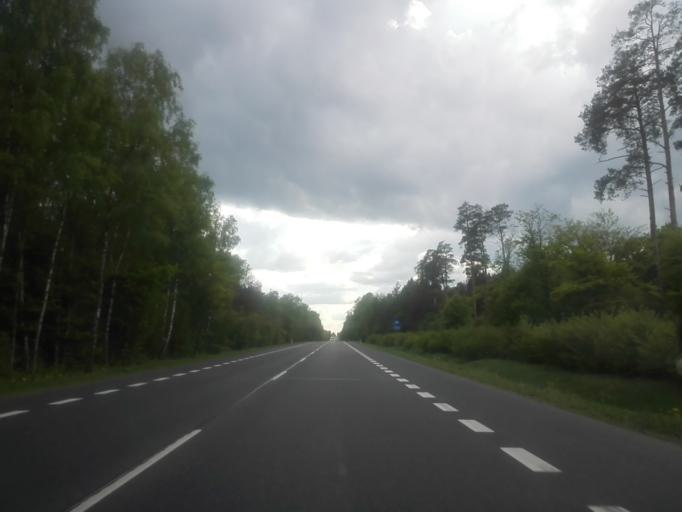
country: PL
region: Masovian Voivodeship
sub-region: Powiat ostrowski
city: Ostrow Mazowiecka
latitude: 52.8370
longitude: 21.9560
